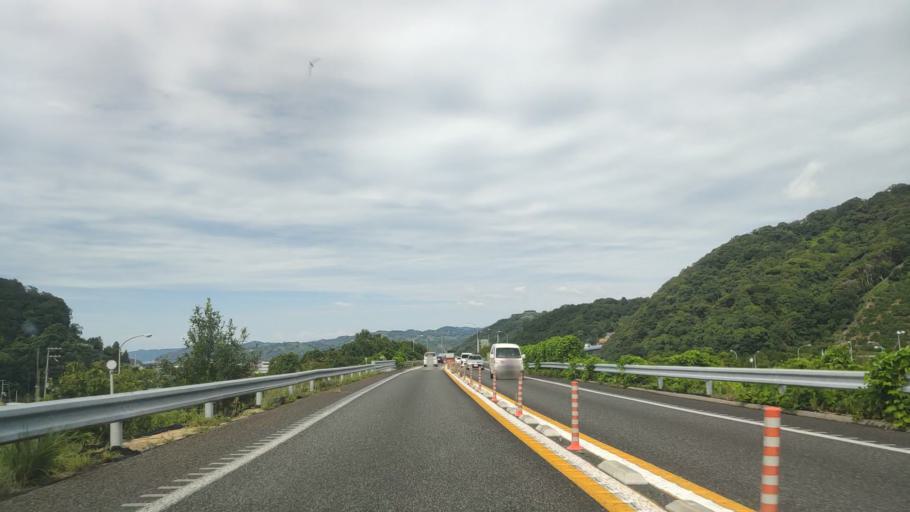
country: JP
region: Wakayama
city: Gobo
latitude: 34.0086
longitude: 135.1914
